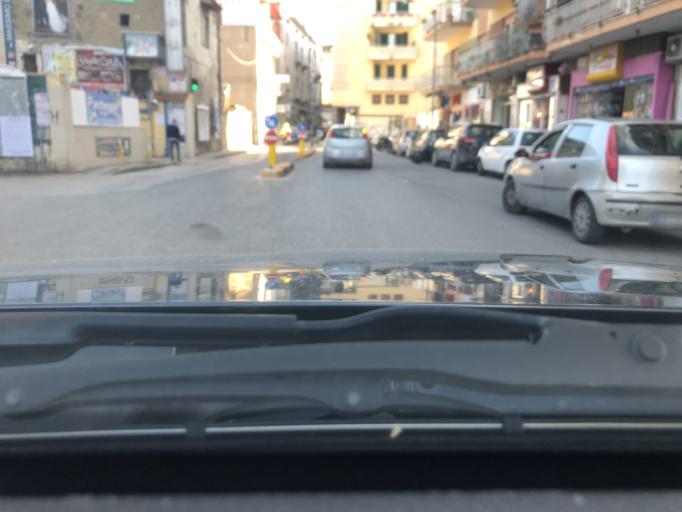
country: IT
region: Campania
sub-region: Provincia di Napoli
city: Calvizzano
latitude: 40.8994
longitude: 14.1892
